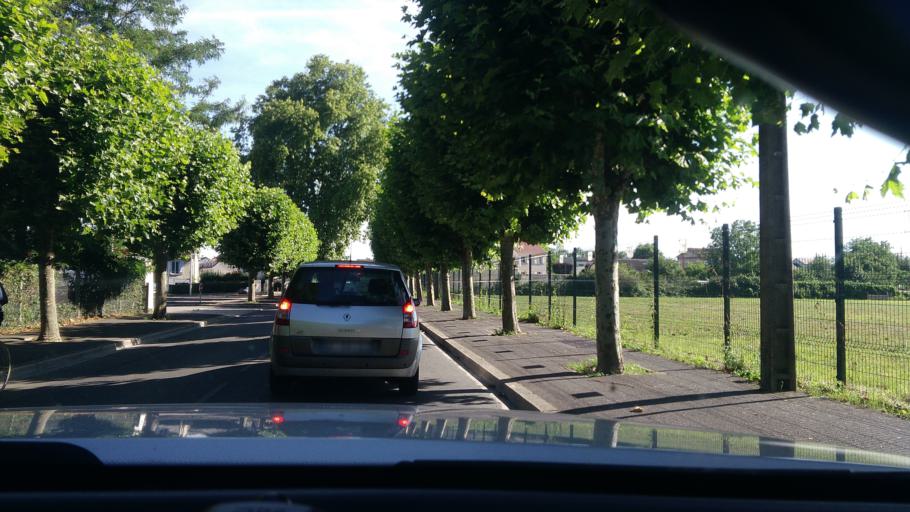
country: FR
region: Ile-de-France
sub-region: Departement de Seine-et-Marne
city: Montereau-Fault-Yonne
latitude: 48.3769
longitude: 2.9453
